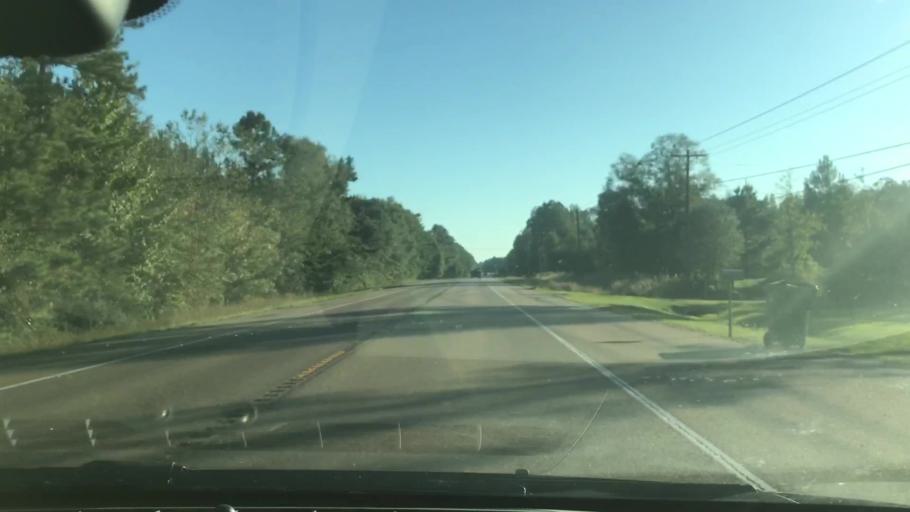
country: US
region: Louisiana
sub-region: Saint Tammany Parish
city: Abita Springs
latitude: 30.5556
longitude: -89.8725
